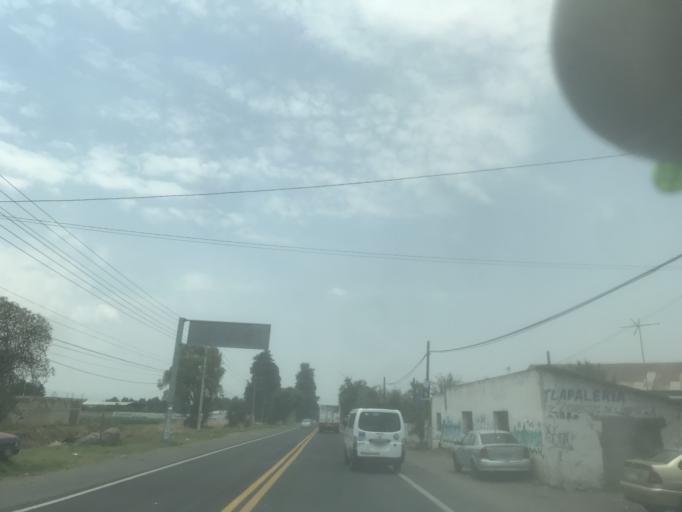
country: MX
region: Mexico
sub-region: Amecameca
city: San Diego Huehuecalco
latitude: 19.0889
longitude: -98.7821
